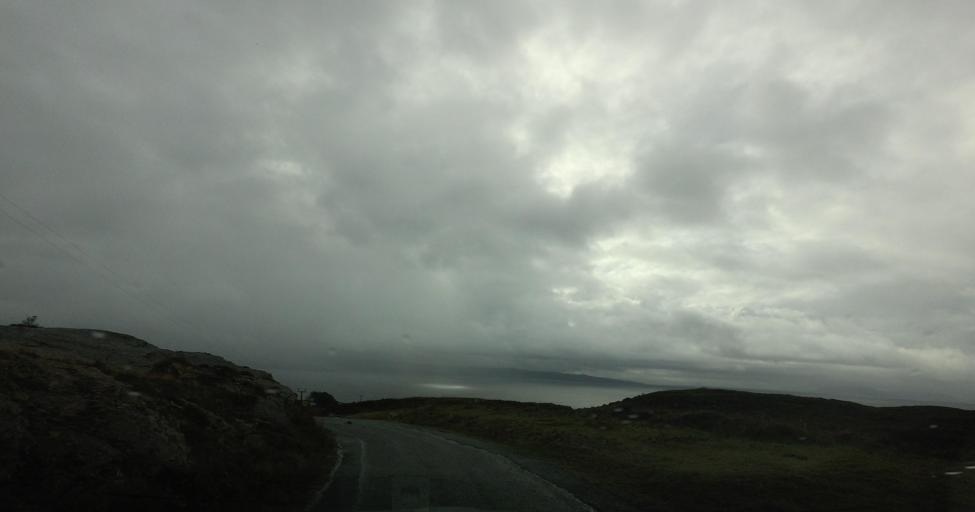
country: GB
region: Scotland
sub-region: Highland
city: Isle of Skye
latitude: 57.1428
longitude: -6.0762
